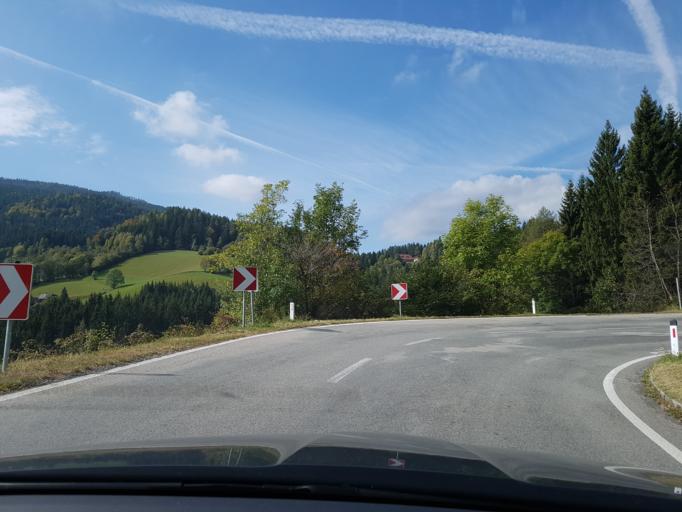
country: AT
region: Carinthia
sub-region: Politischer Bezirk Feldkirchen
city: Himmelberg
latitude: 46.7692
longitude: 14.0110
